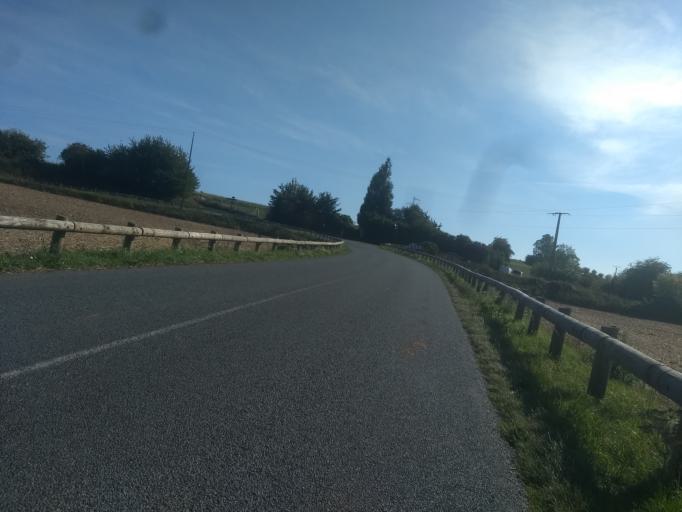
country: FR
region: Nord-Pas-de-Calais
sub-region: Departement du Pas-de-Calais
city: Roeux
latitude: 50.2883
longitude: 2.8993
